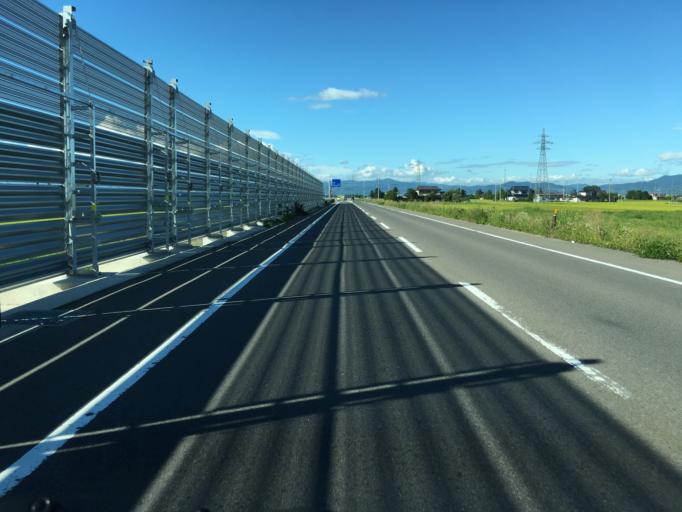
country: JP
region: Yamagata
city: Yonezawa
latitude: 37.9526
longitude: 140.1124
